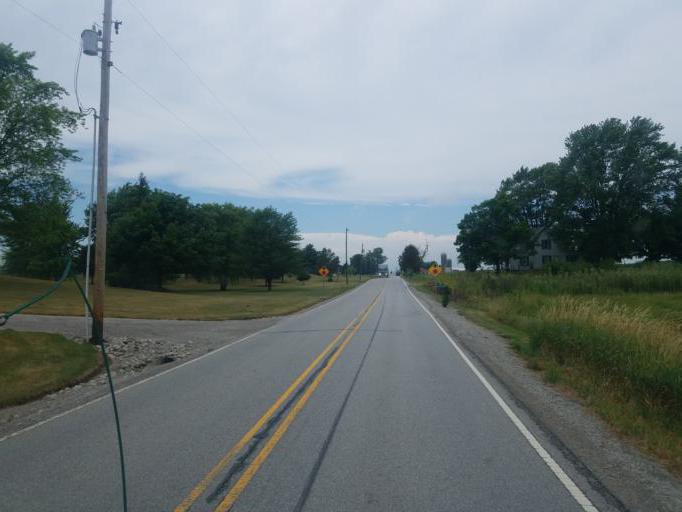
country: US
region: Indiana
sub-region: DeKalb County
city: Butler
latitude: 41.3859
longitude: -84.8667
